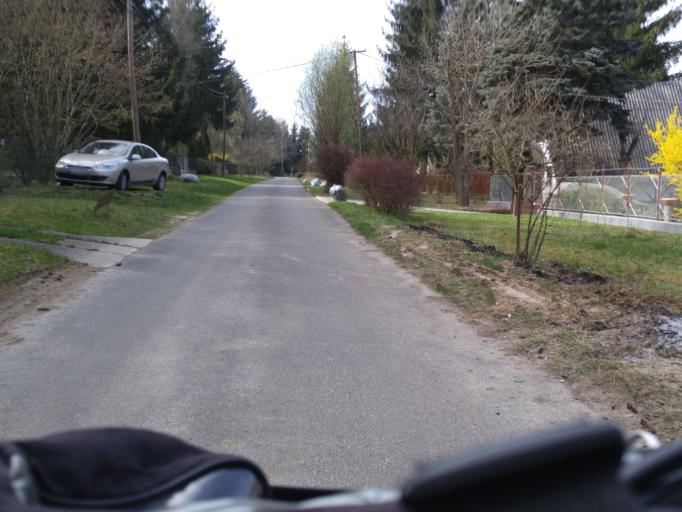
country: HU
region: Nograd
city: Retsag
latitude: 47.9192
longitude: 19.1775
